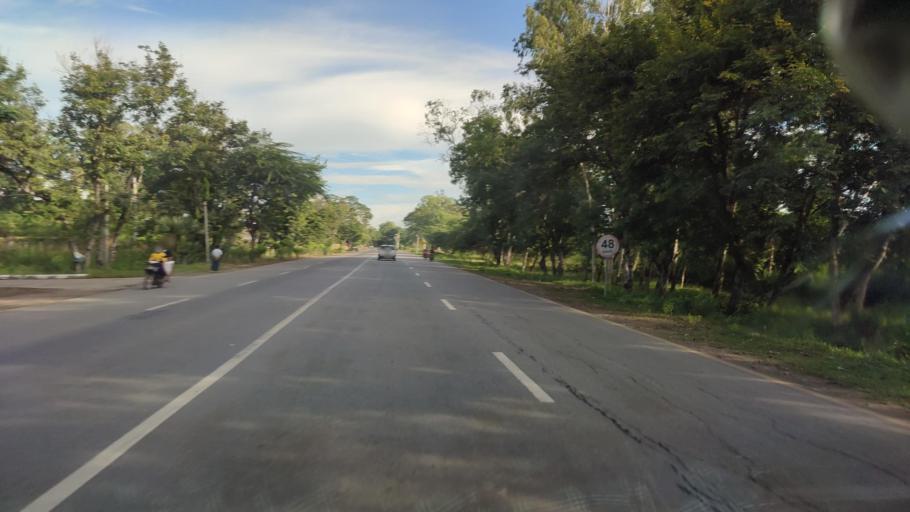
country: MM
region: Mandalay
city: Yamethin
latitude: 20.1486
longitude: 96.1930
